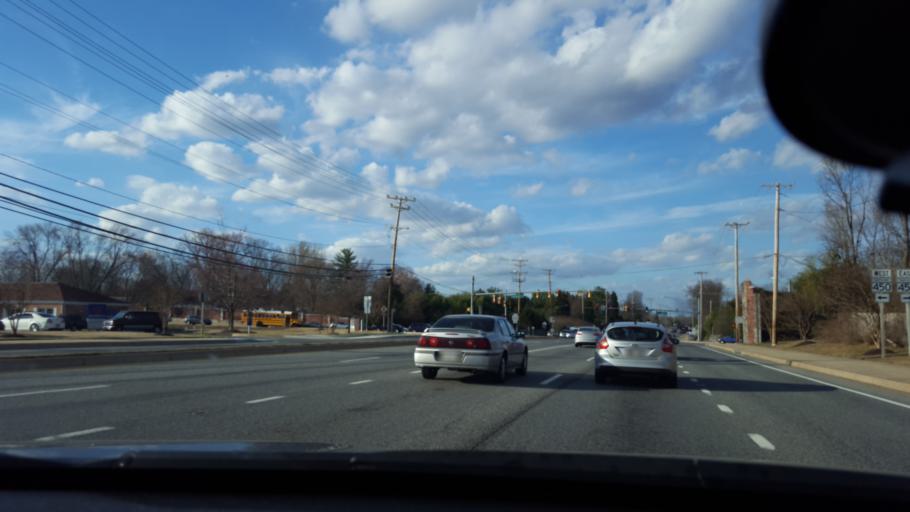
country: US
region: Maryland
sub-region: Prince George's County
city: Bowie
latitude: 38.9729
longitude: -76.7557
